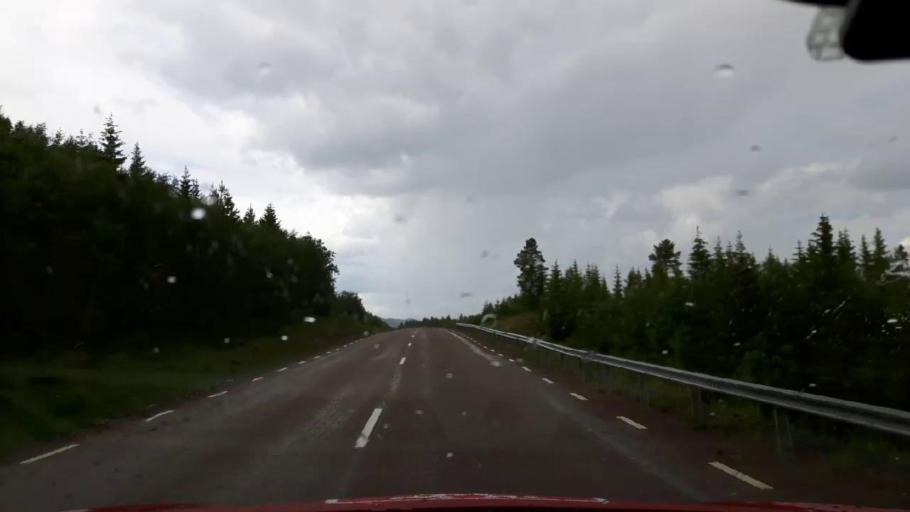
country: SE
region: Jaemtland
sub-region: Krokoms Kommun
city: Valla
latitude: 63.8870
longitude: 14.2786
